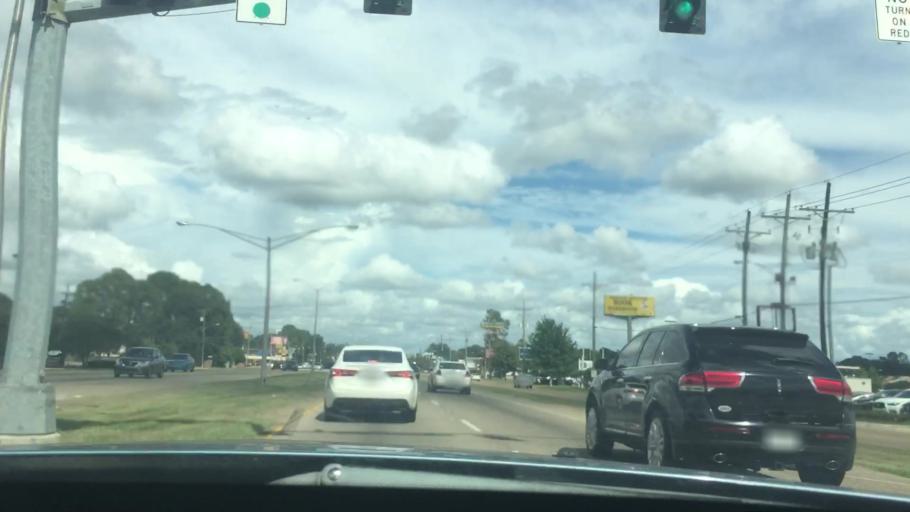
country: US
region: Louisiana
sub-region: East Baton Rouge Parish
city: Westminster
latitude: 30.4544
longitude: -91.0865
